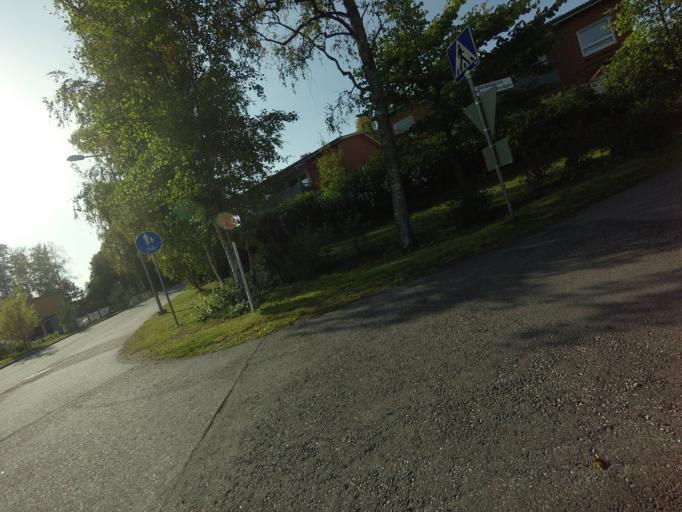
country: FI
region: Uusimaa
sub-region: Helsinki
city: Espoo
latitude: 60.1710
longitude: 24.6438
